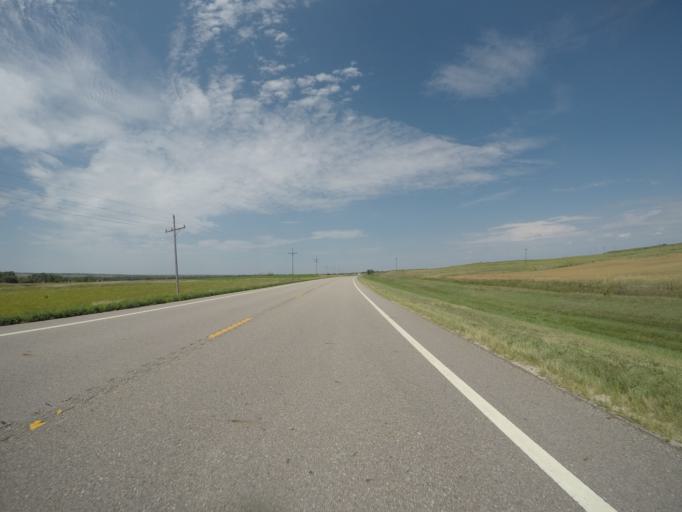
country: US
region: Kansas
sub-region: Rooks County
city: Stockton
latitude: 39.4446
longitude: -99.1629
